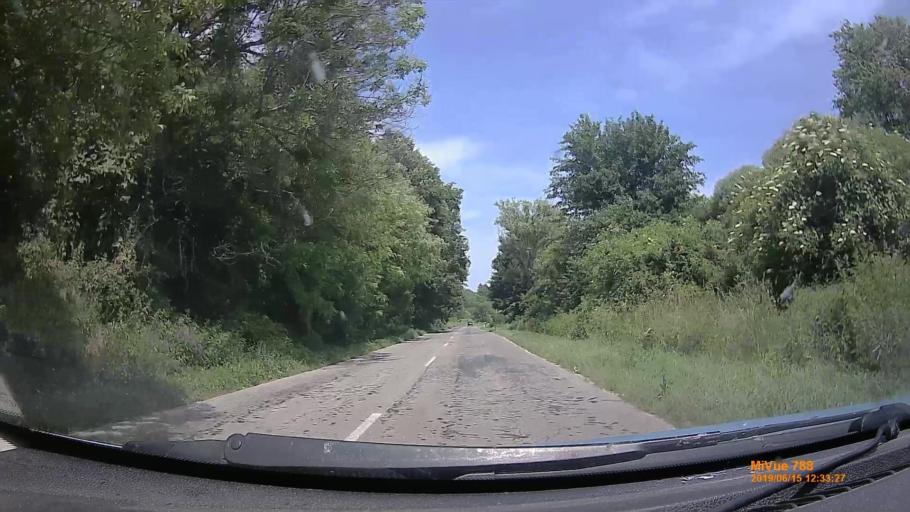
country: HU
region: Baranya
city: Buekkoesd
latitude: 46.1484
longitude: 18.0630
